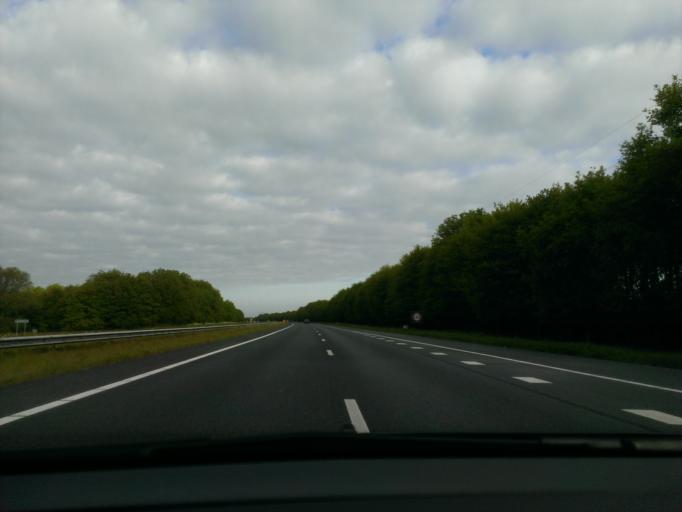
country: NL
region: Overijssel
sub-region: Gemeente Borne
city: Borne
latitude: 52.3121
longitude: 6.6951
